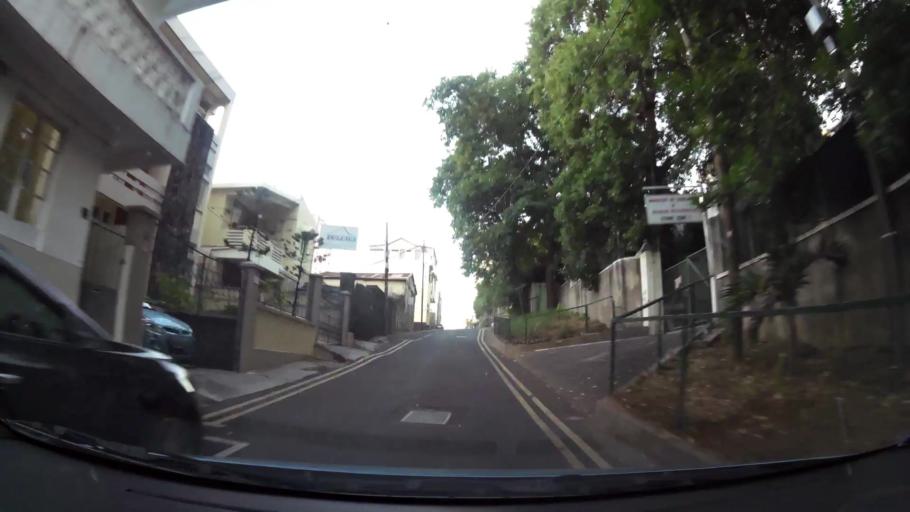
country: MU
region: Port Louis
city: Port Louis
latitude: -20.1630
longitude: 57.5076
